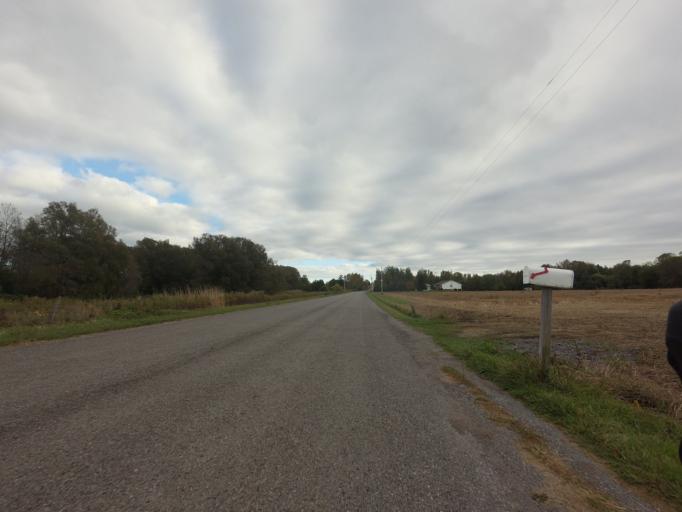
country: CA
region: Ontario
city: Cobourg
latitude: 43.9765
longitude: -78.0648
